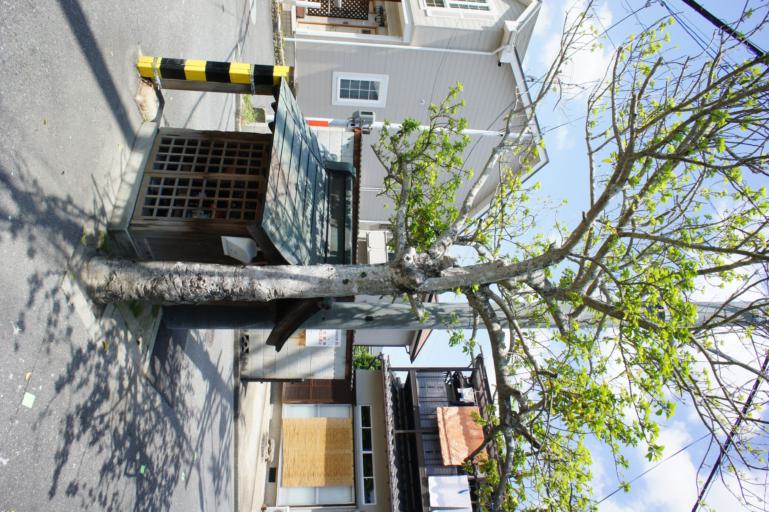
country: JP
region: Nara
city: Tenri
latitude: 34.6220
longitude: 135.7848
